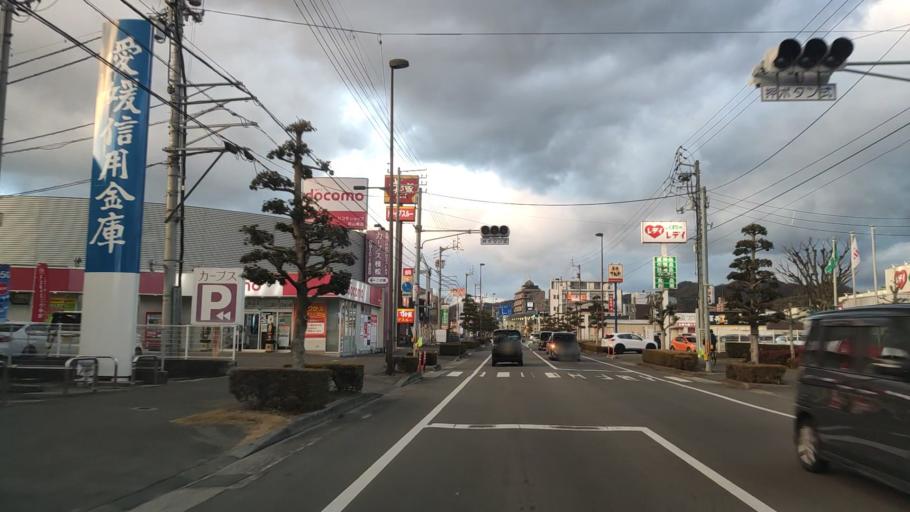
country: JP
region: Ehime
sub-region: Shikoku-chuo Shi
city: Matsuyama
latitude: 33.8355
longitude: 132.7870
